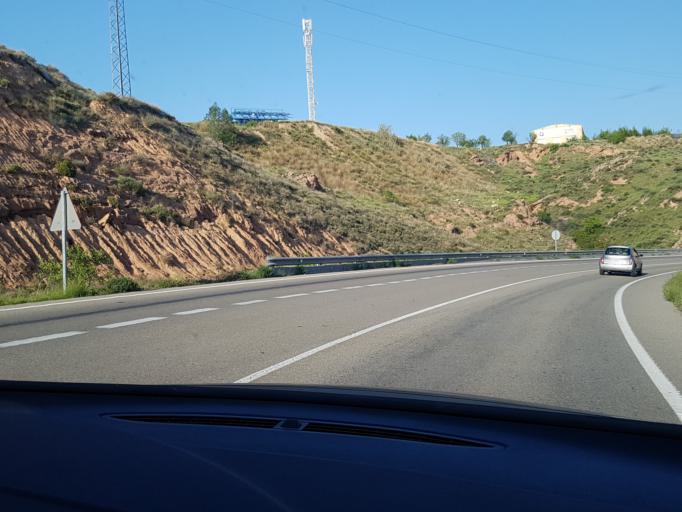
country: ES
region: La Rioja
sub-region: Provincia de La Rioja
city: Arnedo
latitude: 42.2390
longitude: -2.0878
